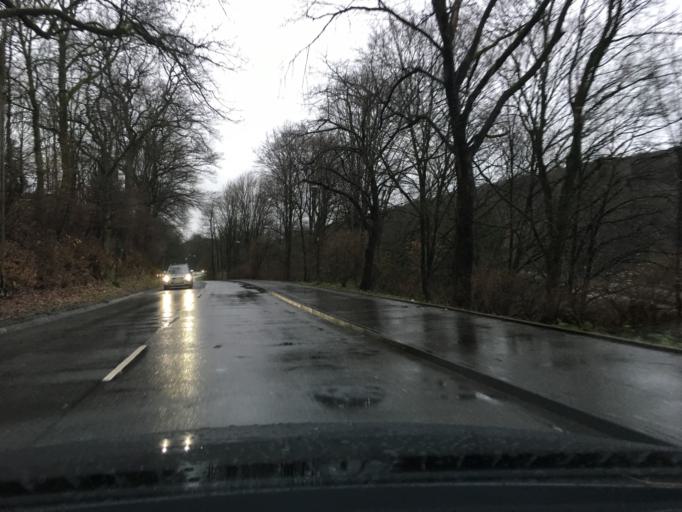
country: DE
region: North Rhine-Westphalia
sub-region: Regierungsbezirk Dusseldorf
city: Velbert
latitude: 51.3473
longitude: 7.1051
